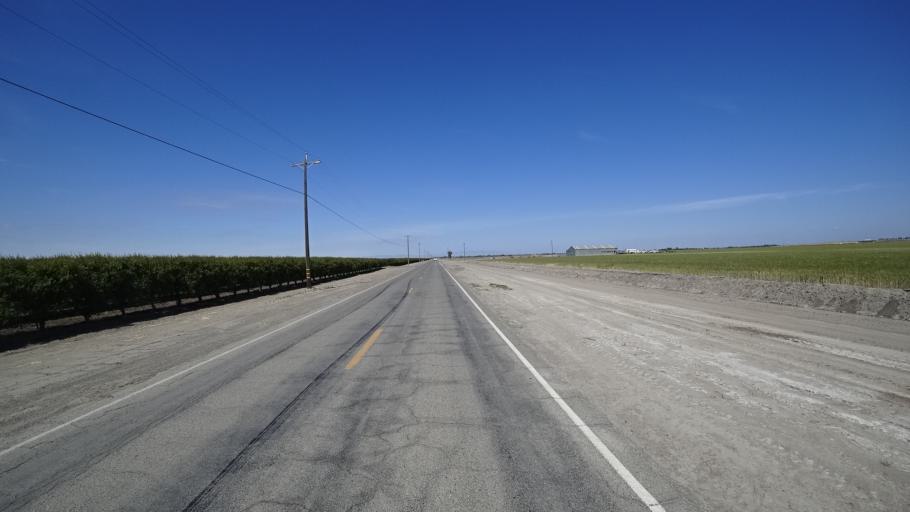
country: US
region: California
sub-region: Kings County
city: Lemoore
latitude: 36.2551
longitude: -119.8242
